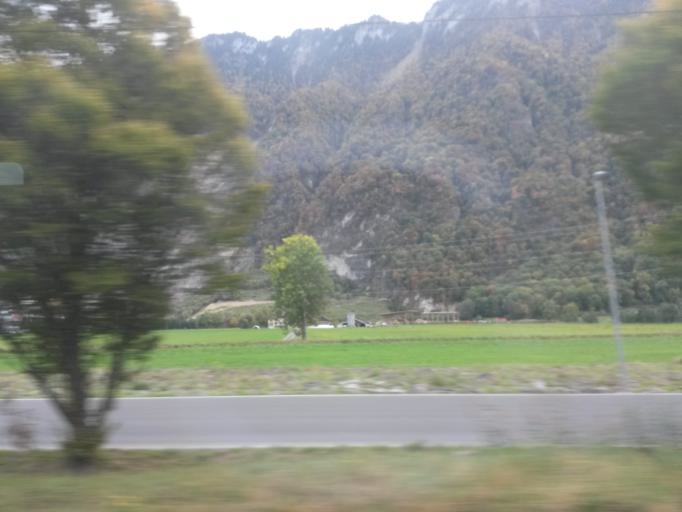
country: CH
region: Vaud
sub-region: Aigle District
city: Villeneuve
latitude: 46.3830
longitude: 6.9284
